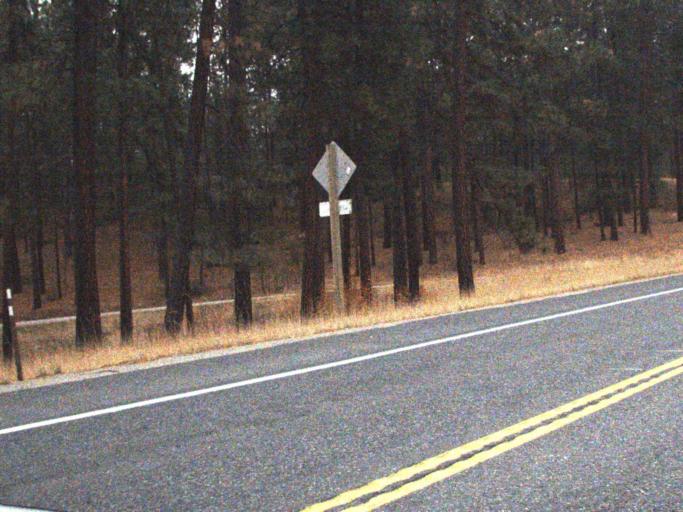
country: US
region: Washington
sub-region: Stevens County
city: Kettle Falls
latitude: 48.6233
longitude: -118.1113
